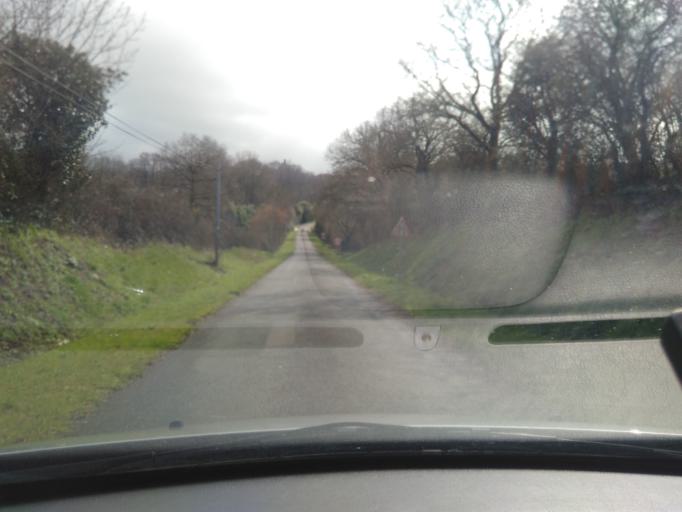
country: FR
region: Pays de la Loire
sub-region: Departement de la Vendee
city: Sainte-Cecile
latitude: 46.7021
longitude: -1.1274
